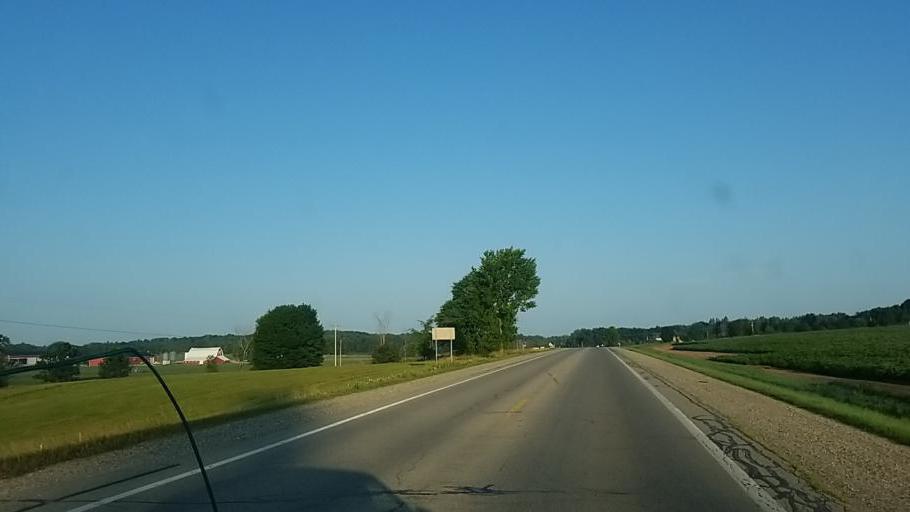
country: US
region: Michigan
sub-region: Montcalm County
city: Lakeview
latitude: 43.4304
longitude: -85.2070
